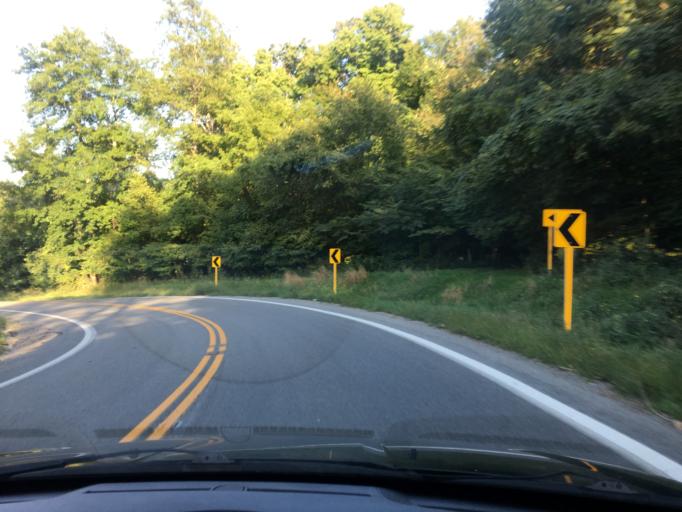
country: US
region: Ohio
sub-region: Logan County
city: West Liberty
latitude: 40.2647
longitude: -83.6677
